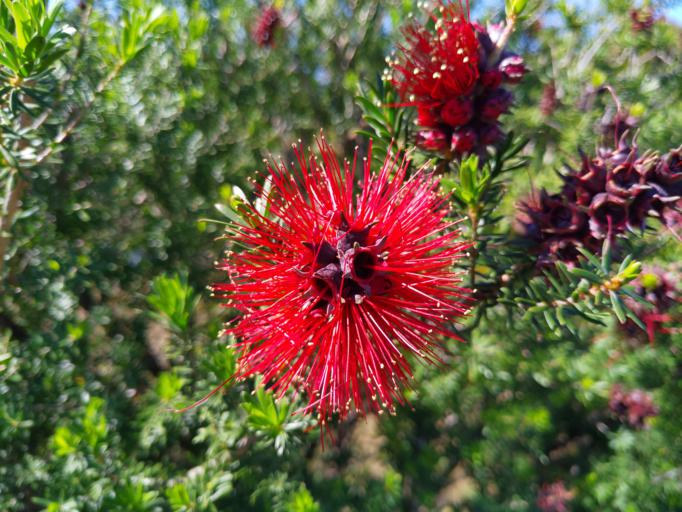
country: AU
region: Western Australia
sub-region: Bunbury
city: Bunbury
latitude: -33.3389
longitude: 115.6340
